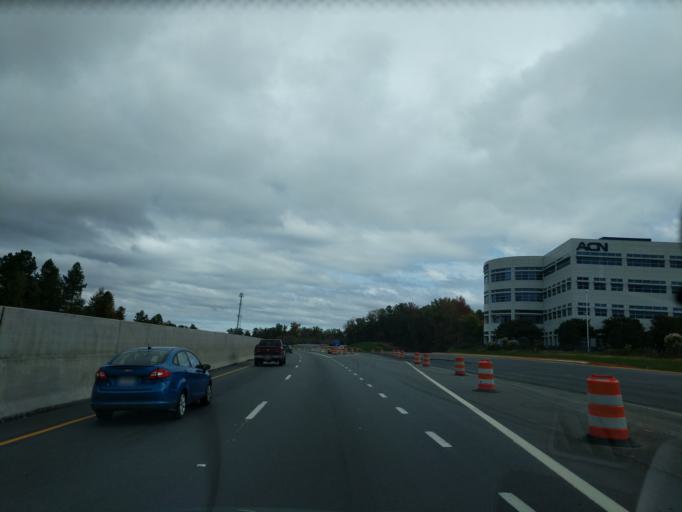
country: US
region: North Carolina
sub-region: Cabarrus County
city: Concord
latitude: 35.4494
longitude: -80.5989
